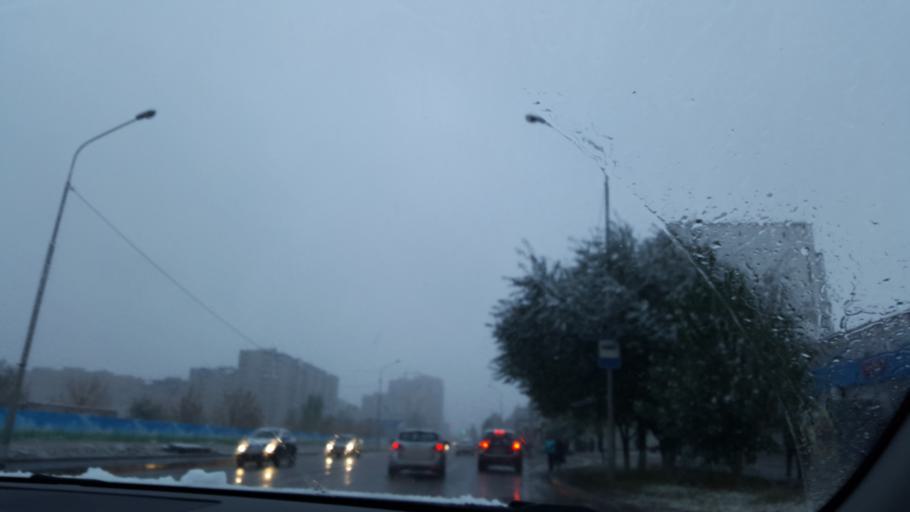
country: KZ
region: Astana Qalasy
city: Astana
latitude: 51.1563
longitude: 71.4993
